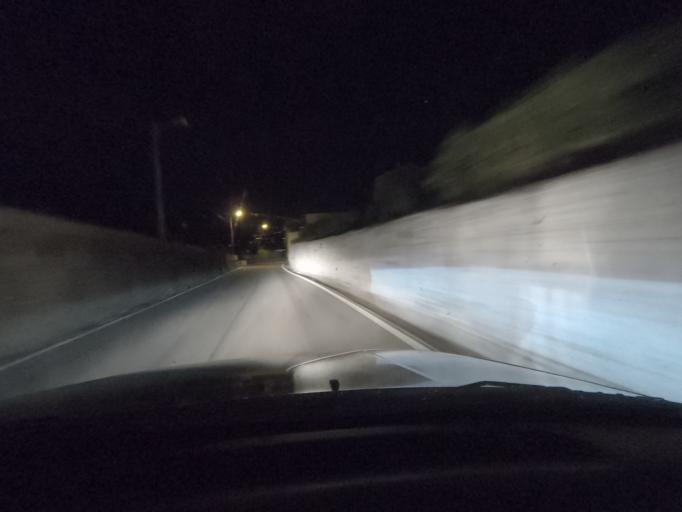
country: PT
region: Vila Real
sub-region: Peso da Regua
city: Godim
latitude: 41.1858
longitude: -7.7932
